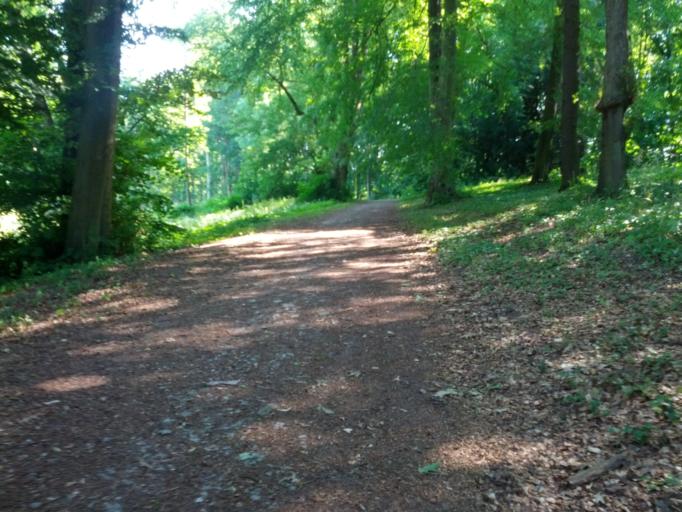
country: DE
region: Thuringia
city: Eisenach
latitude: 50.9717
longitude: 10.3350
